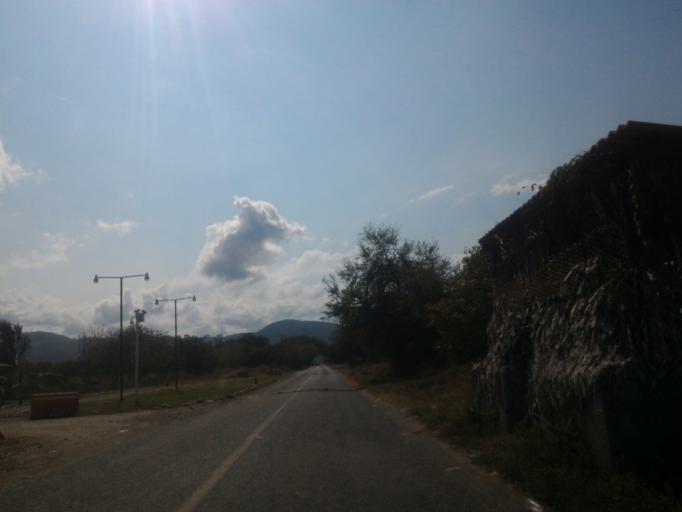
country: MX
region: Michoacan
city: Coahuayana Viejo
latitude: 18.5223
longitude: -103.5851
